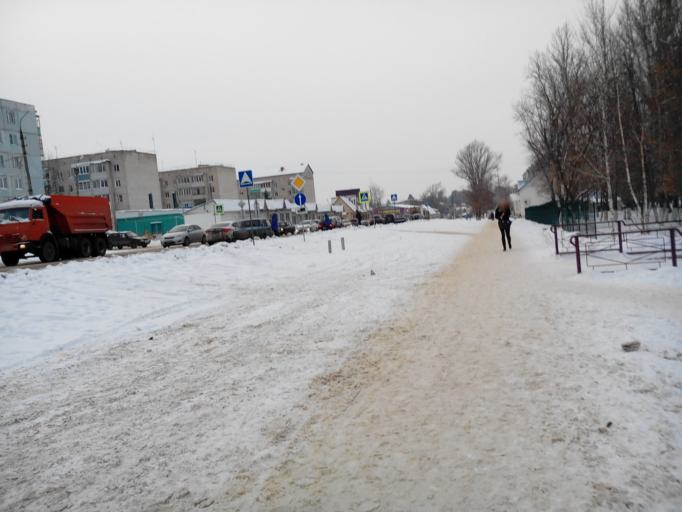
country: RU
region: Tula
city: Yefremov
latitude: 53.1489
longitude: 38.0805
